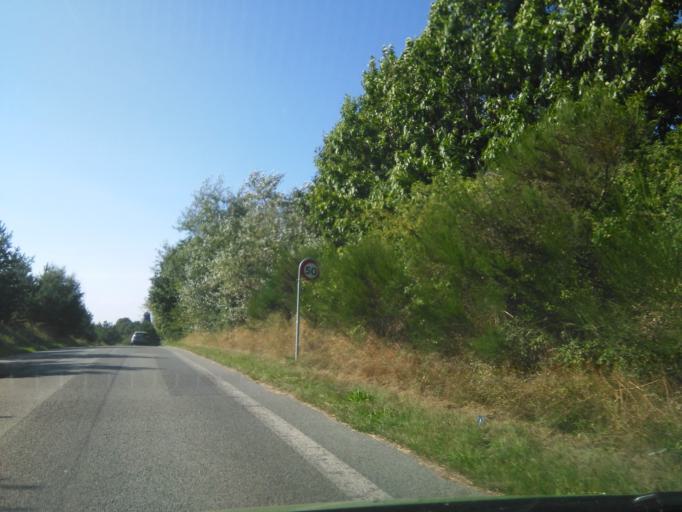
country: DK
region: Central Jutland
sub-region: Syddjurs Kommune
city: Ebeltoft
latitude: 56.2008
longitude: 10.6925
